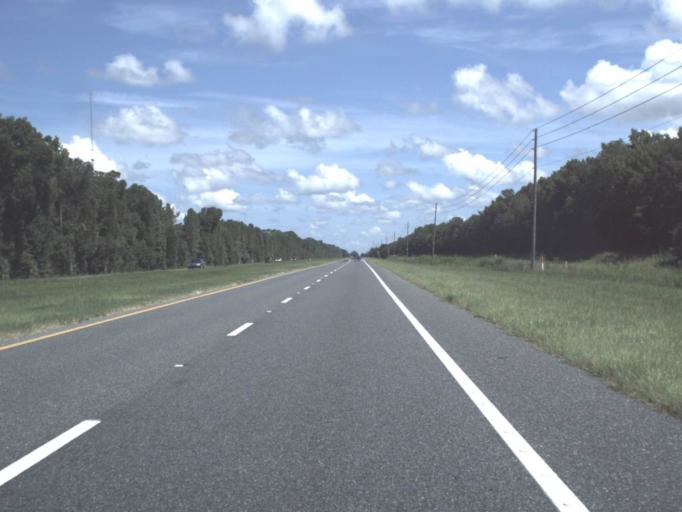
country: US
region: Florida
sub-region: Levy County
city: Inglis
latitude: 29.2143
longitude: -82.6994
